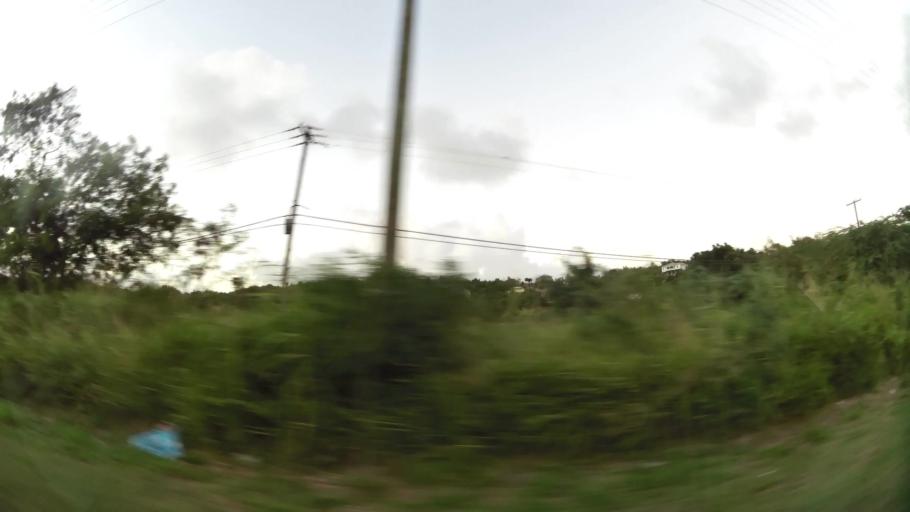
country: AG
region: Saint George
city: Piggotts
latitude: 17.1304
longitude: -61.8060
